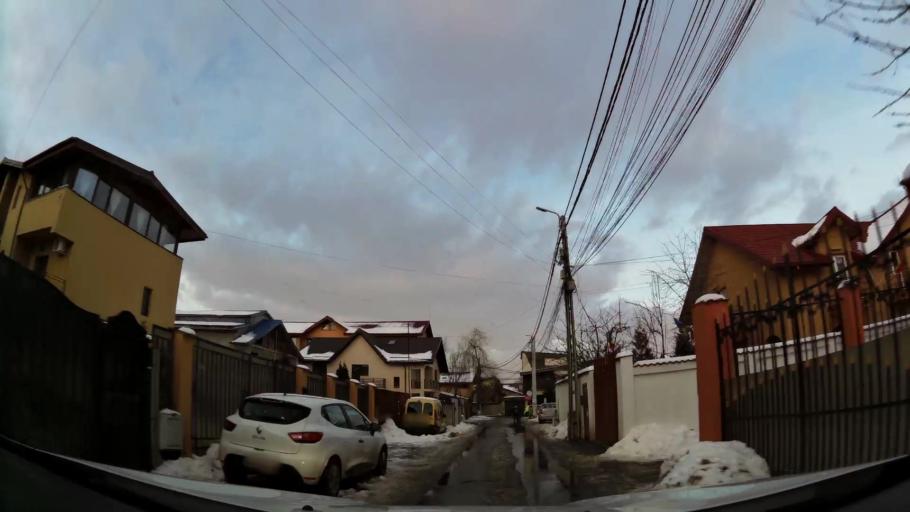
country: RO
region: Ilfov
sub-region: Comuna Popesti-Leordeni
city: Popesti-Leordeni
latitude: 44.3769
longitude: 26.1501
